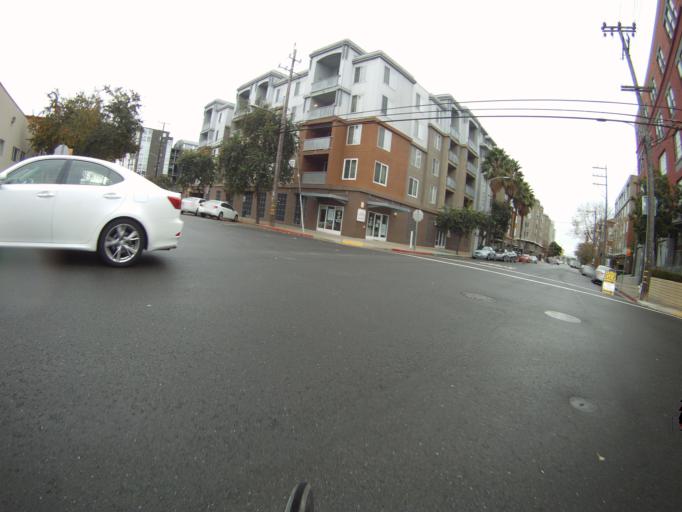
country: US
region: California
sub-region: Alameda County
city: Oakland
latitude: 37.7951
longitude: -122.2694
